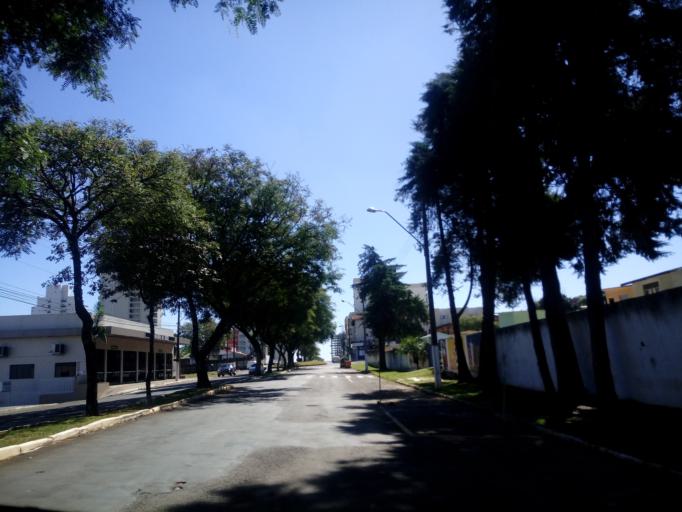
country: BR
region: Santa Catarina
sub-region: Chapeco
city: Chapeco
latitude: -27.1130
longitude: -52.6141
